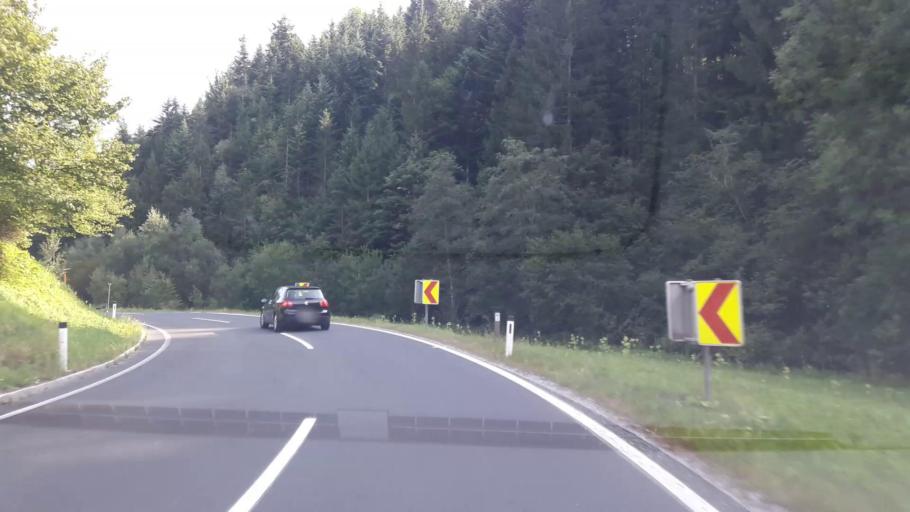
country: AT
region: Styria
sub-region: Politischer Bezirk Weiz
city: Birkfeld
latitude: 47.3380
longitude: 15.6855
